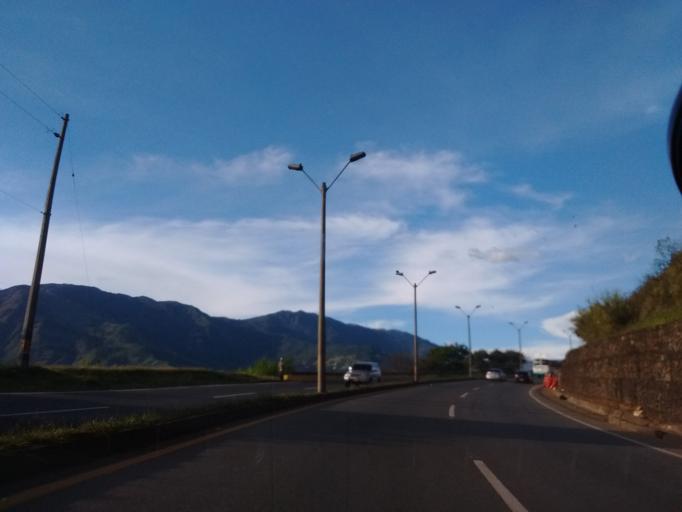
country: CO
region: Antioquia
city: Bello
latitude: 6.3203
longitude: -75.5469
